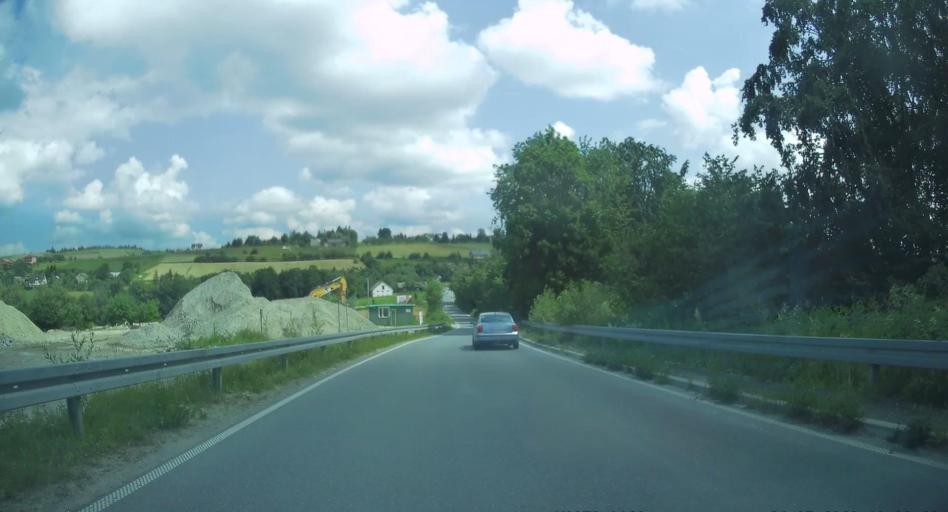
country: PL
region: Lesser Poland Voivodeship
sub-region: Powiat nowosadecki
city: Korzenna
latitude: 49.7006
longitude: 20.7607
